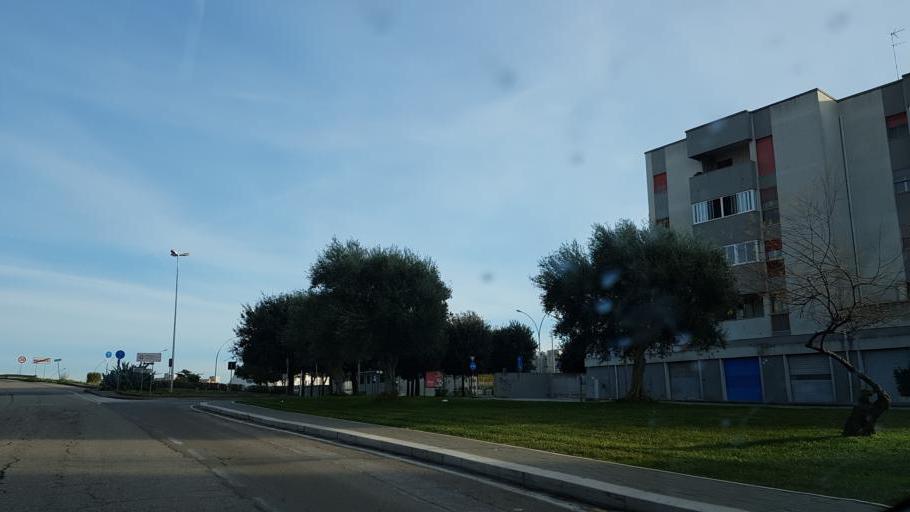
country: IT
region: Apulia
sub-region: Provincia di Brindisi
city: Brindisi
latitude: 40.6267
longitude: 17.9423
